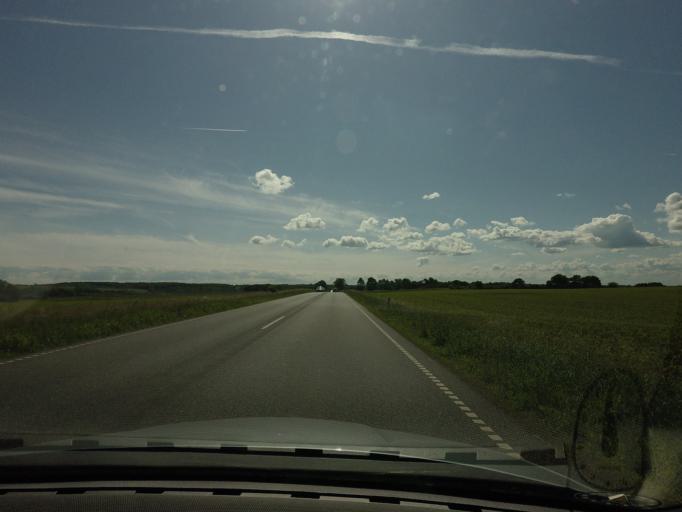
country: DK
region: Central Jutland
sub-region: Syddjurs Kommune
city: Ebeltoft
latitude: 56.3366
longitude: 10.7384
